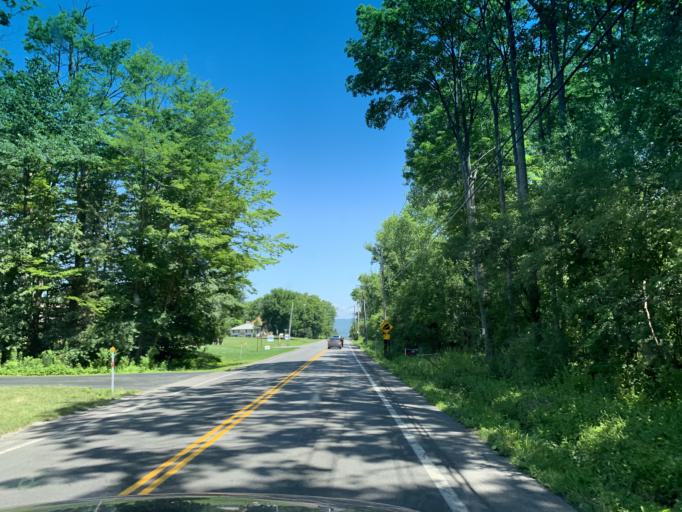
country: US
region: New York
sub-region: Oneida County
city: Washington Mills
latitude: 43.0614
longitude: -75.2452
